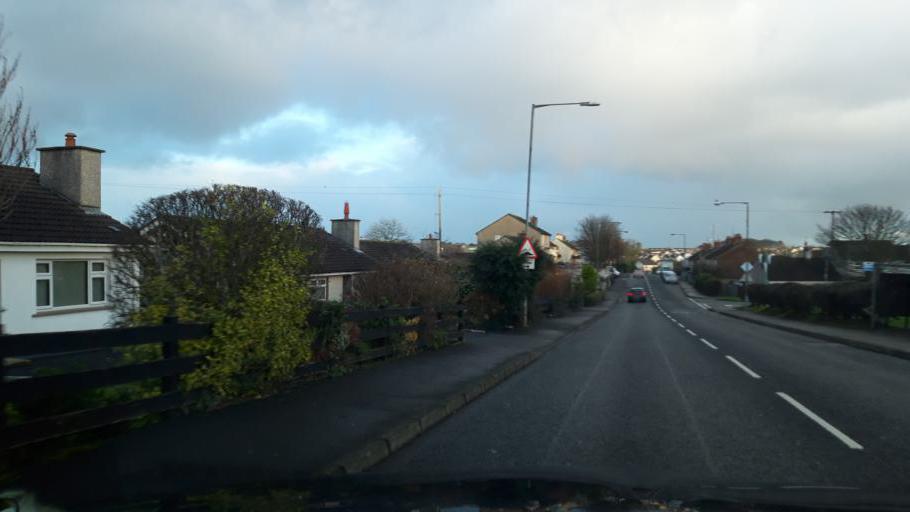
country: GB
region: Northern Ireland
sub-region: Moyle District
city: Ballycastle
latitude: 55.1974
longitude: -6.2619
